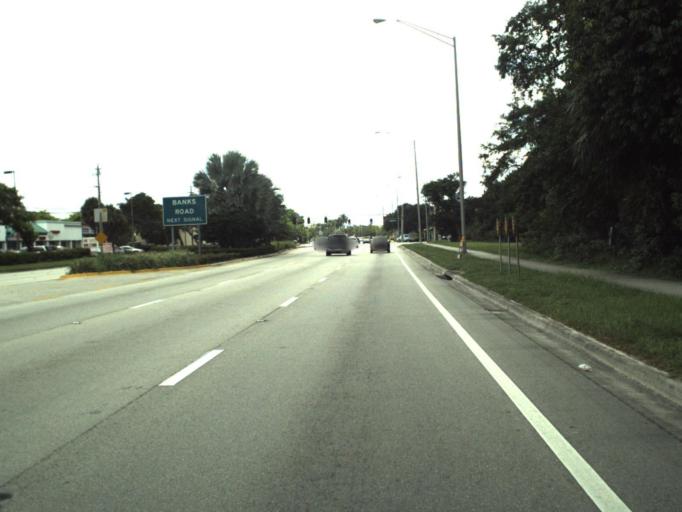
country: US
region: Florida
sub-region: Broward County
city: Margate
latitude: 26.2340
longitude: -80.1923
